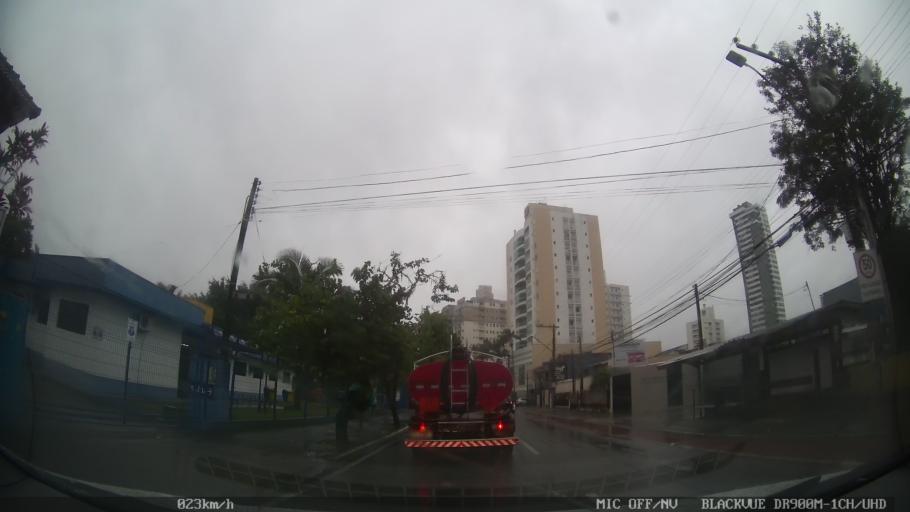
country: BR
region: Santa Catarina
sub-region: Itajai
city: Itajai
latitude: -26.9102
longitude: -48.6787
